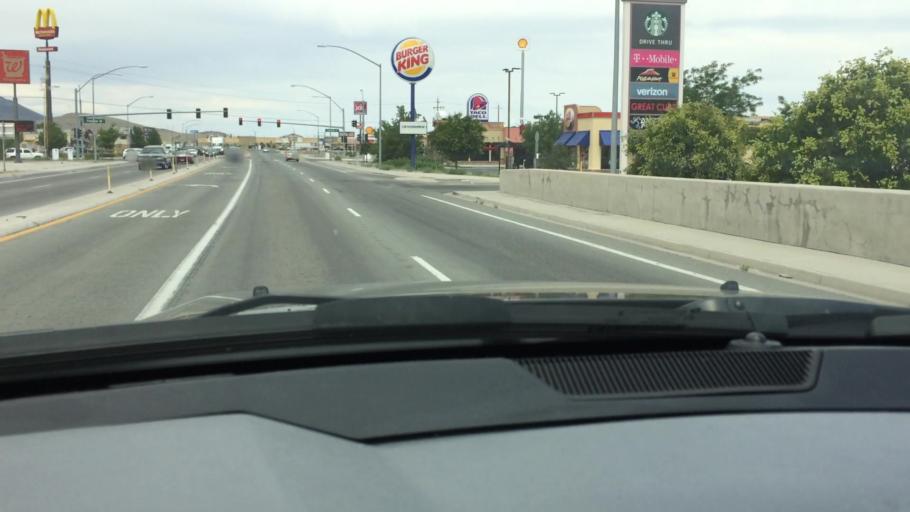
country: US
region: Nevada
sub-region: Lyon County
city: Fernley
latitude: 39.6069
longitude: -119.2234
